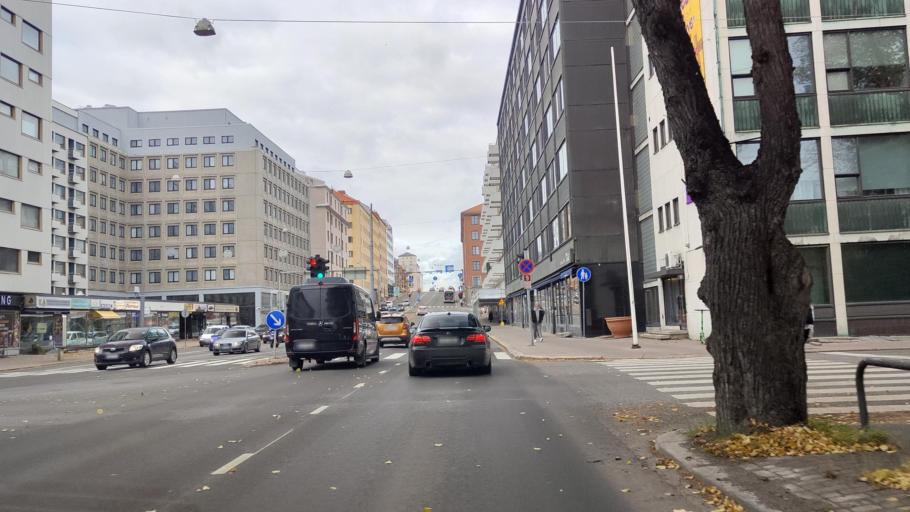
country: FI
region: Varsinais-Suomi
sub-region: Turku
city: Turku
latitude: 60.4530
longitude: 22.2740
